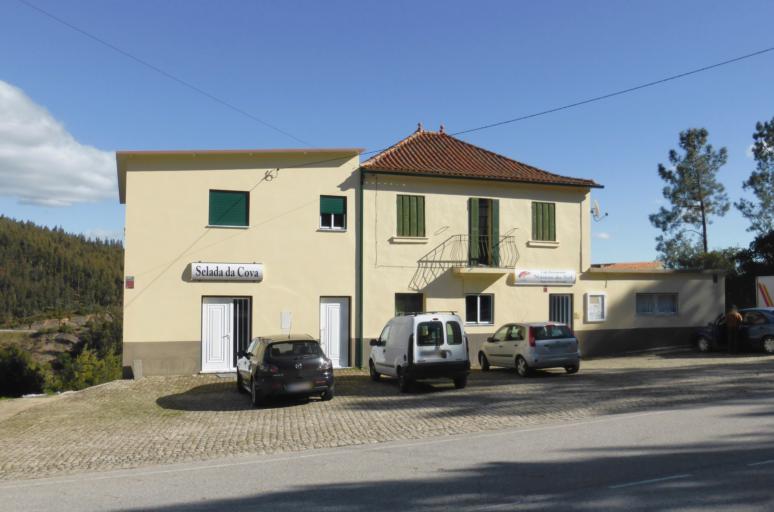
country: PT
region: Coimbra
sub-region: Pampilhosa da Serra
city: Pampilhosa da Serra
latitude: 40.0470
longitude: -7.8716
